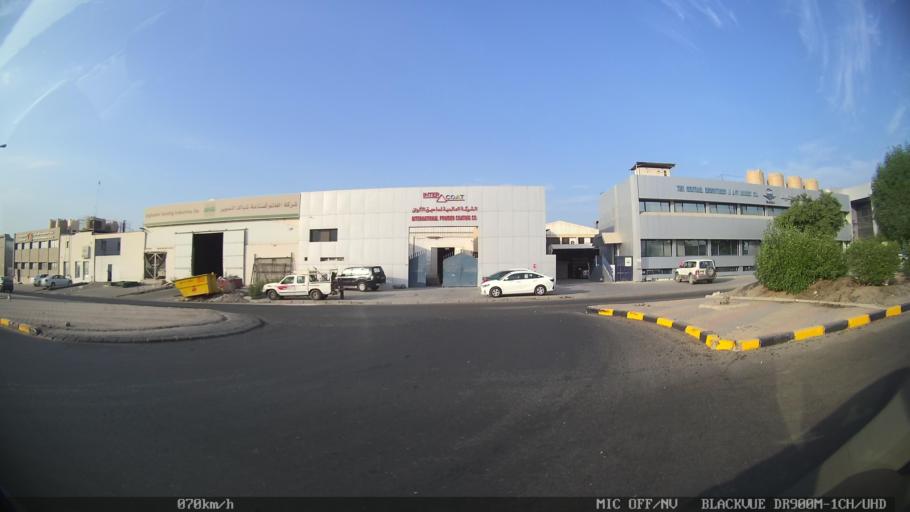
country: KW
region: Al Farwaniyah
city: Janub as Surrah
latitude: 29.2240
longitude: 48.0050
